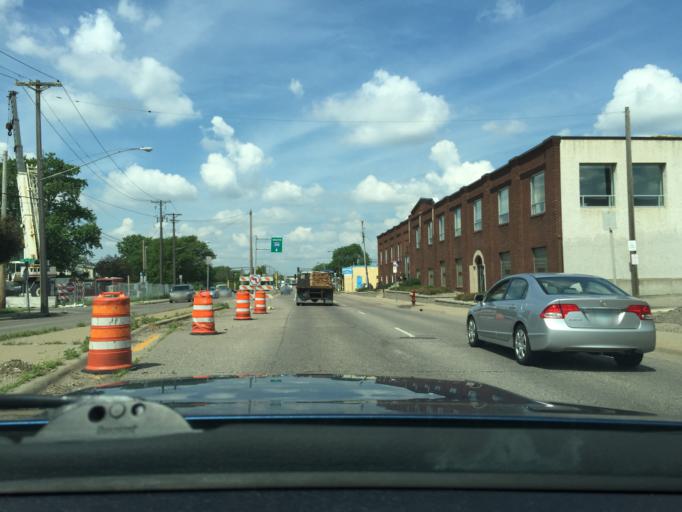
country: US
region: Minnesota
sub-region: Ramsey County
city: Lauderdale
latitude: 44.9915
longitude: -93.2339
